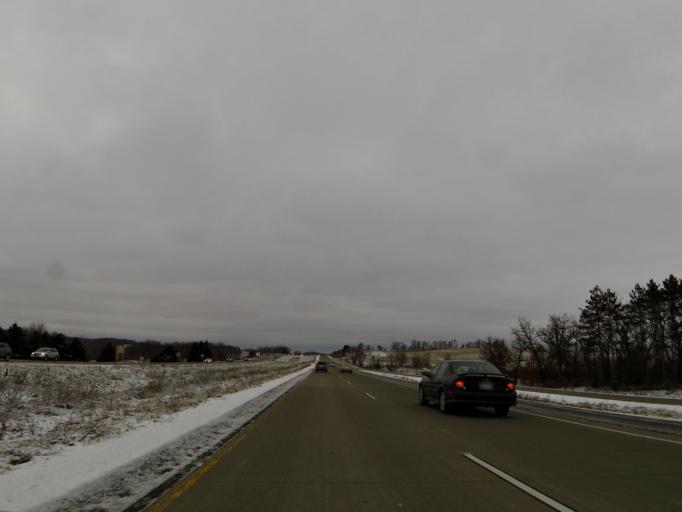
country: US
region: Wisconsin
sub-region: Trempealeau County
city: Osseo
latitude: 44.6438
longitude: -91.3062
